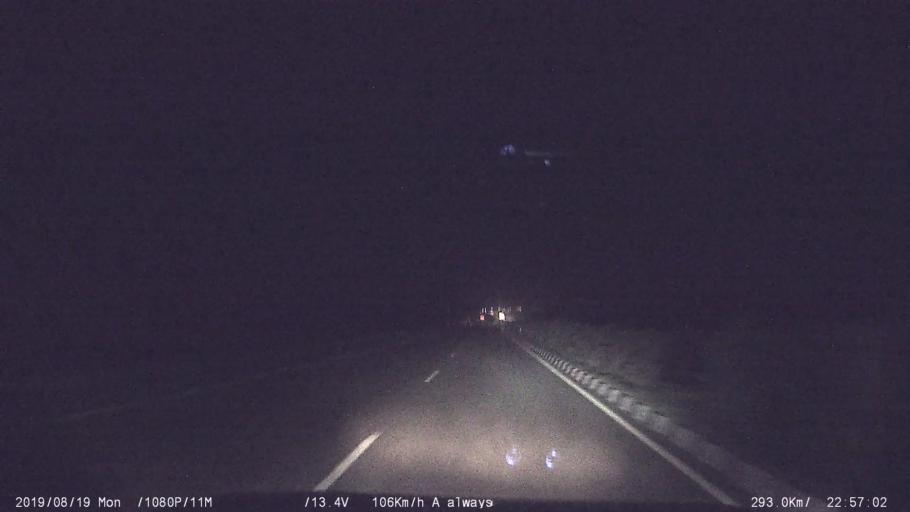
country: IN
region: Tamil Nadu
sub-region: Erode
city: Perundurai
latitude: 11.2778
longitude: 77.5563
